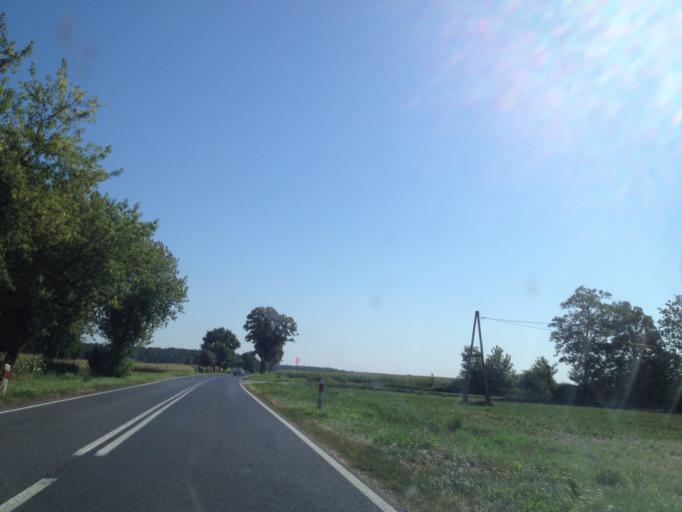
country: PL
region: Greater Poland Voivodeship
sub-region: Powiat sredzki
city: Zaniemysl
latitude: 52.1410
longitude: 17.1127
